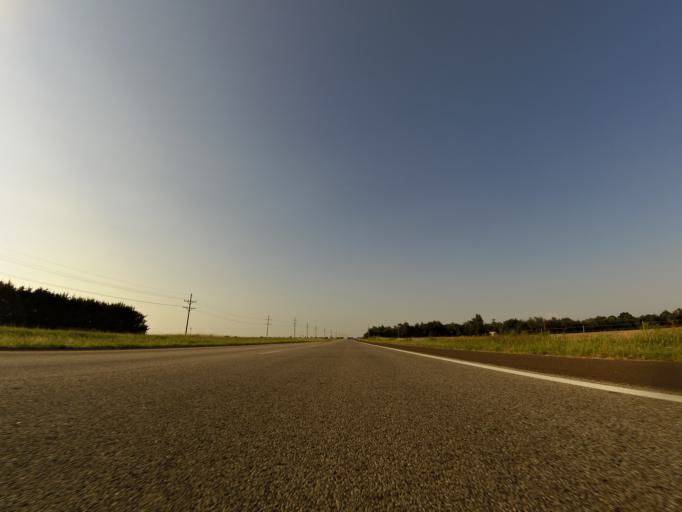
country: US
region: Kansas
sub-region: Reno County
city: South Hutchinson
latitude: 37.9821
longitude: -97.9403
